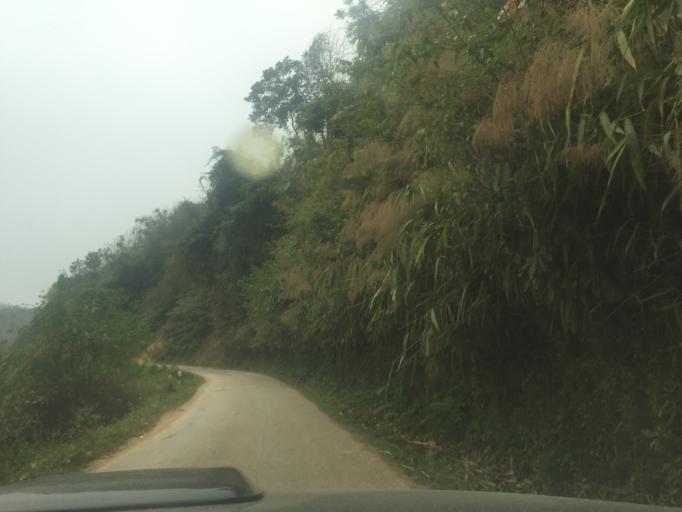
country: LA
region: Vientiane
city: Muang Sanakham
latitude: 18.3946
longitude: 101.5183
